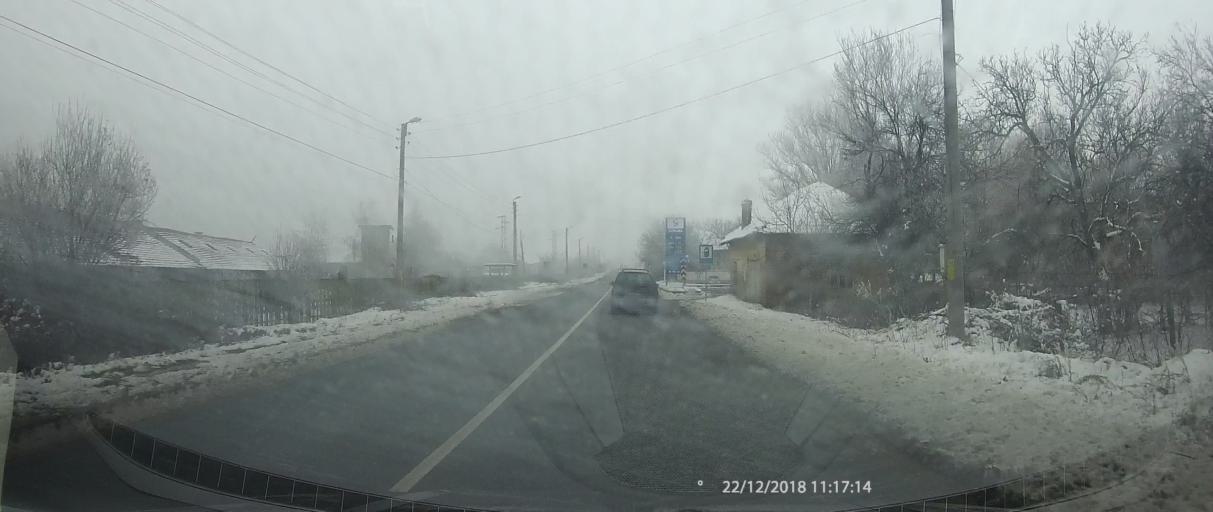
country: BG
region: Kyustendil
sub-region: Obshtina Kyustendil
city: Kyustendil
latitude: 42.2749
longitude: 22.7562
